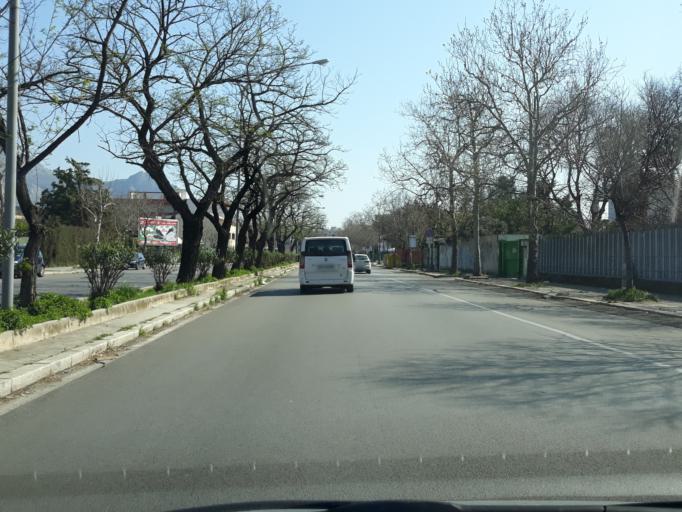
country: IT
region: Sicily
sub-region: Palermo
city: Palermo
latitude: 38.1383
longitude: 13.3249
